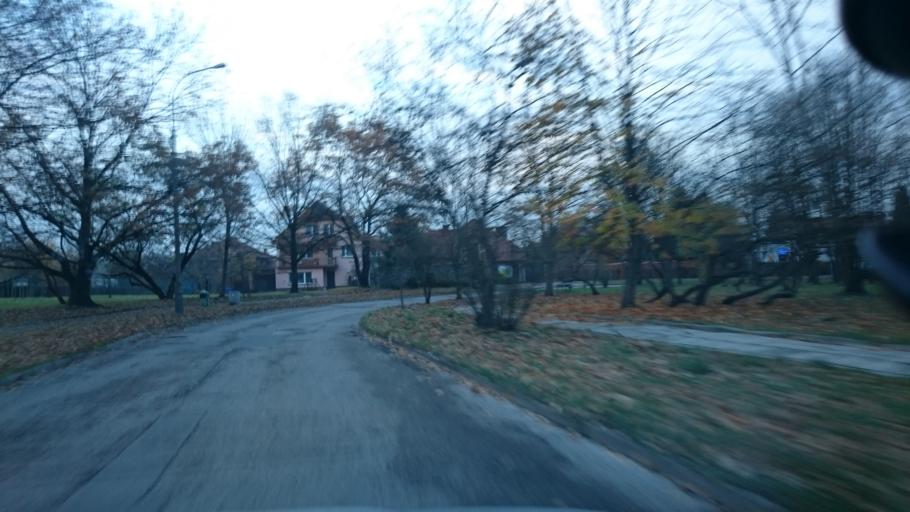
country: PL
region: Lesser Poland Voivodeship
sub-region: Powiat wielicki
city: Czarnochowice
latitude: 50.0195
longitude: 20.0131
